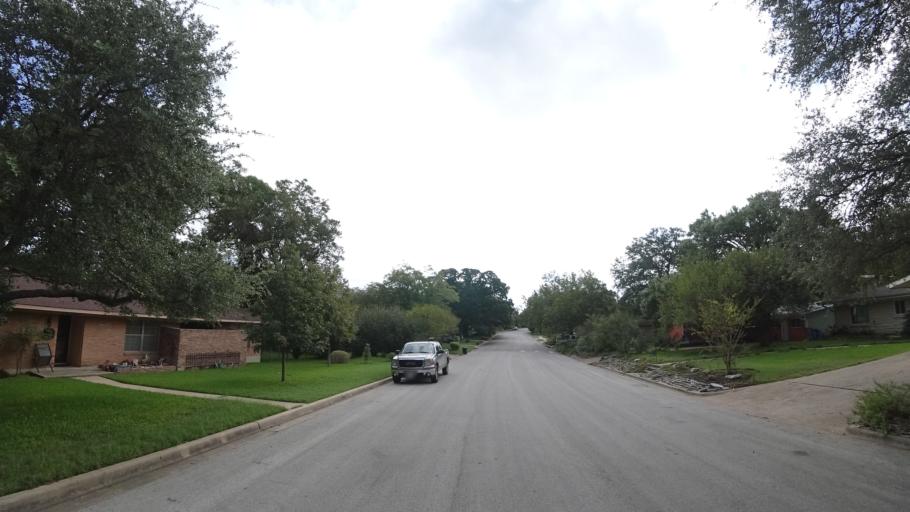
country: US
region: Texas
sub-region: Travis County
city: West Lake Hills
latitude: 30.3471
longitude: -97.7406
